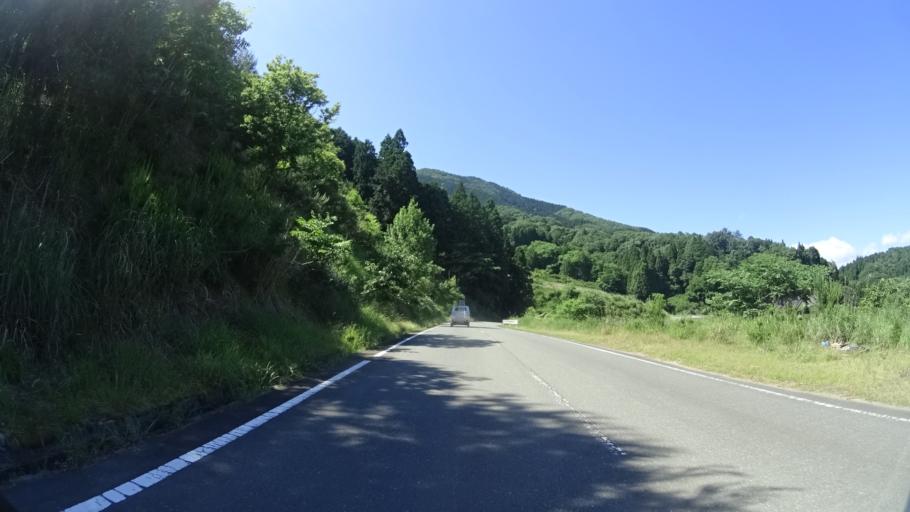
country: JP
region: Kyoto
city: Fukuchiyama
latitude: 35.3864
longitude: 135.0690
